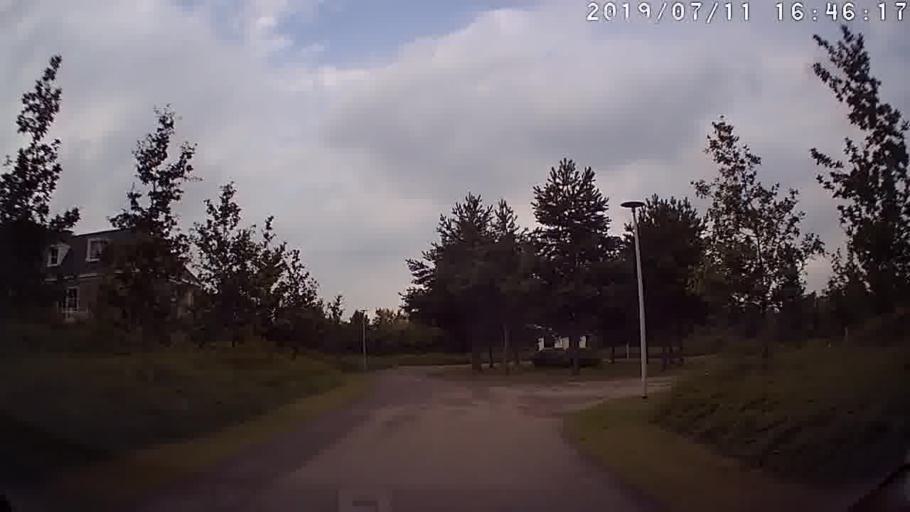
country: NL
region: Overijssel
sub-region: Gemeente Zwolle
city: Zwolle
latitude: 52.4808
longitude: 6.1283
